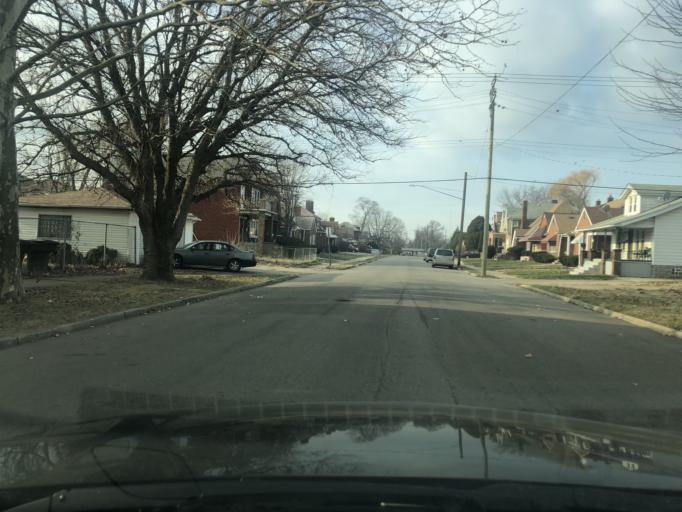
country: US
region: Michigan
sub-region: Wayne County
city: Highland Park
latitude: 42.3977
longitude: -83.1218
